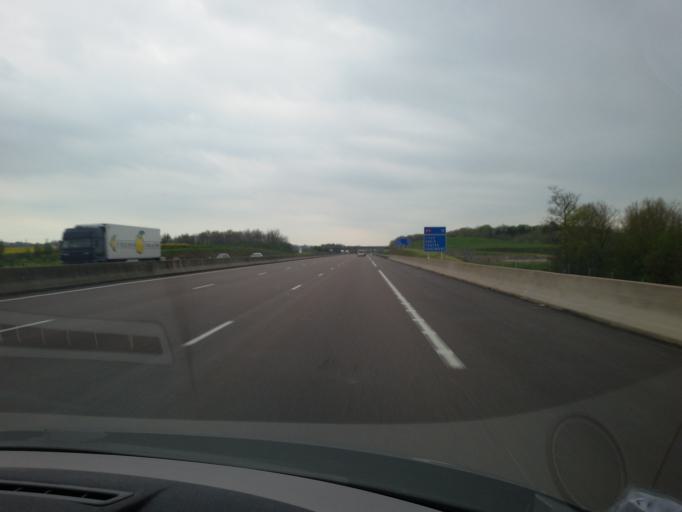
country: FR
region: Champagne-Ardenne
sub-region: Departement de la Haute-Marne
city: Langres
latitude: 47.8239
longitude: 5.2257
